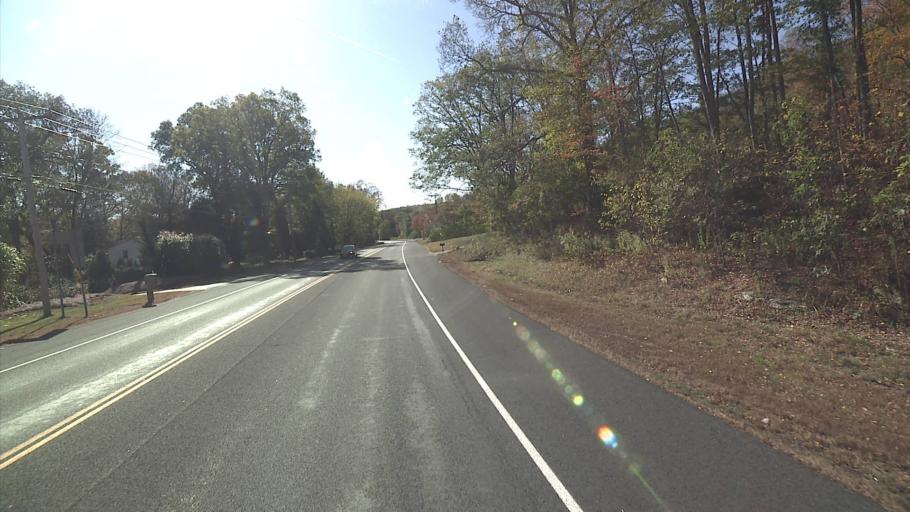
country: US
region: Connecticut
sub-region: Tolland County
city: Coventry Lake
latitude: 41.7672
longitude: -72.4063
